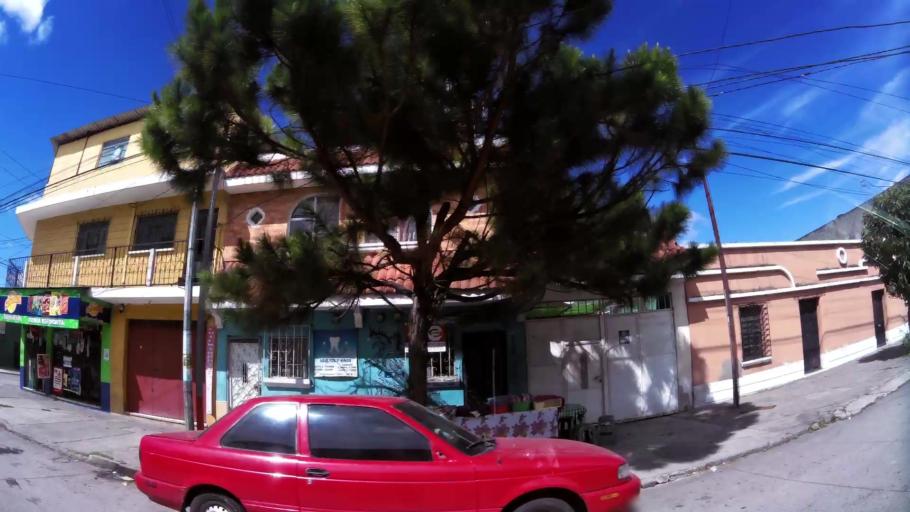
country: GT
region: Guatemala
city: Guatemala City
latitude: 14.5981
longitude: -90.5457
